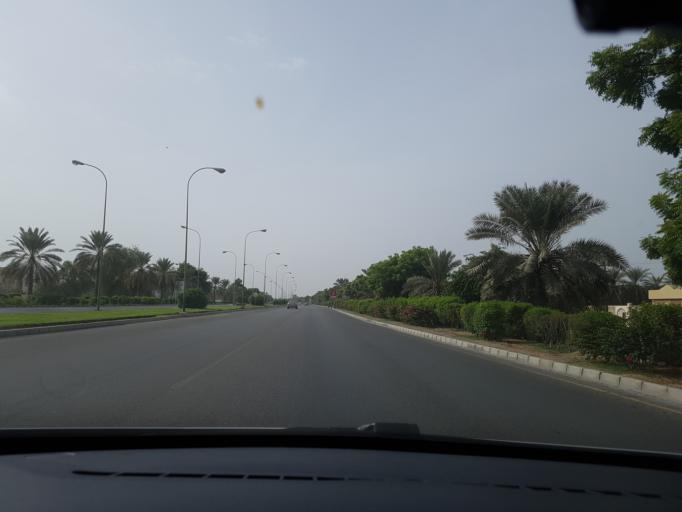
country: OM
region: Al Batinah
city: Al Sohar
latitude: 24.3770
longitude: 56.7030
